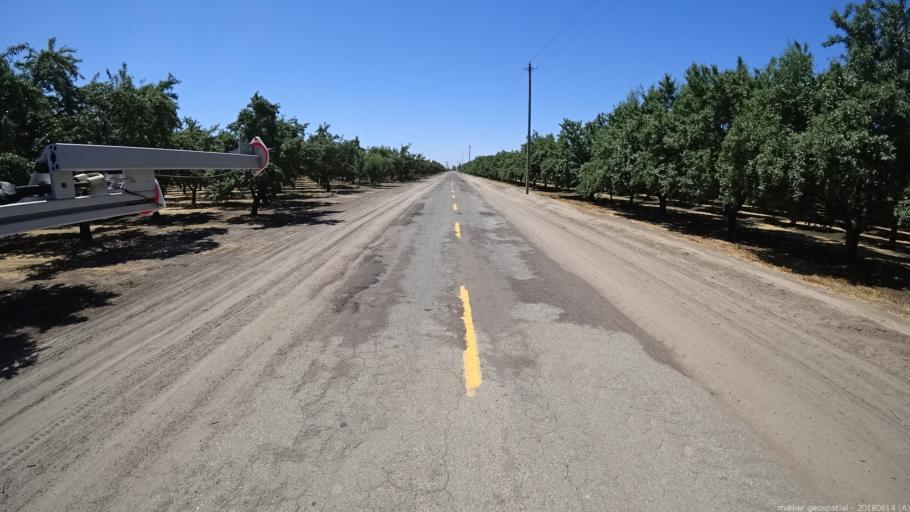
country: US
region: California
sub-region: Madera County
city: Fairmead
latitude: 36.9994
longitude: -120.2476
